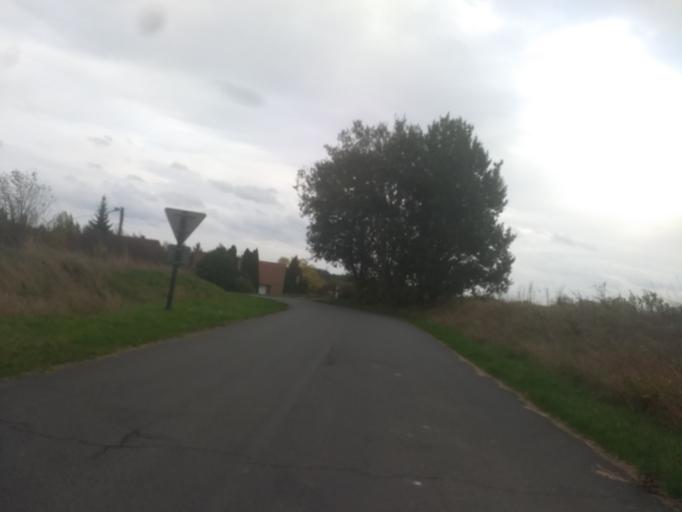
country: FR
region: Nord-Pas-de-Calais
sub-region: Departement du Pas-de-Calais
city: Achicourt
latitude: 50.2717
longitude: 2.7467
